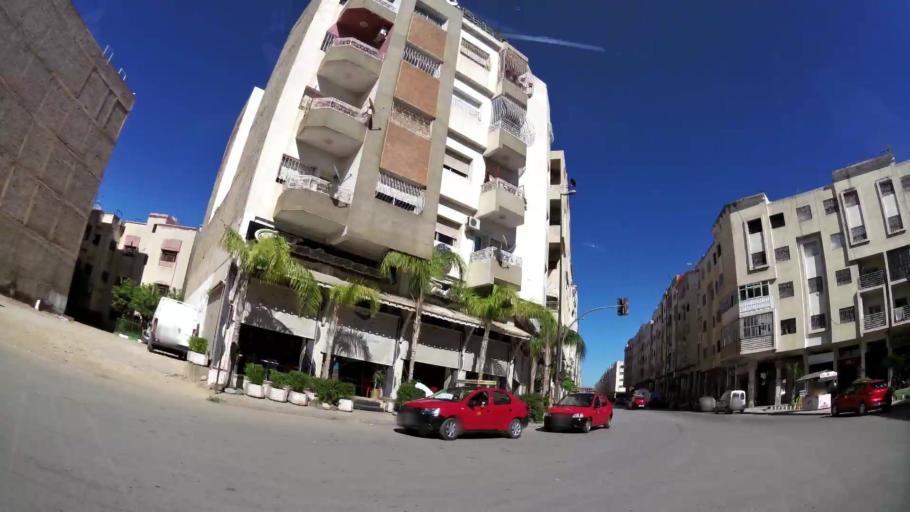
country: MA
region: Fes-Boulemane
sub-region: Fes
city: Fes
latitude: 34.0182
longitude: -4.9814
